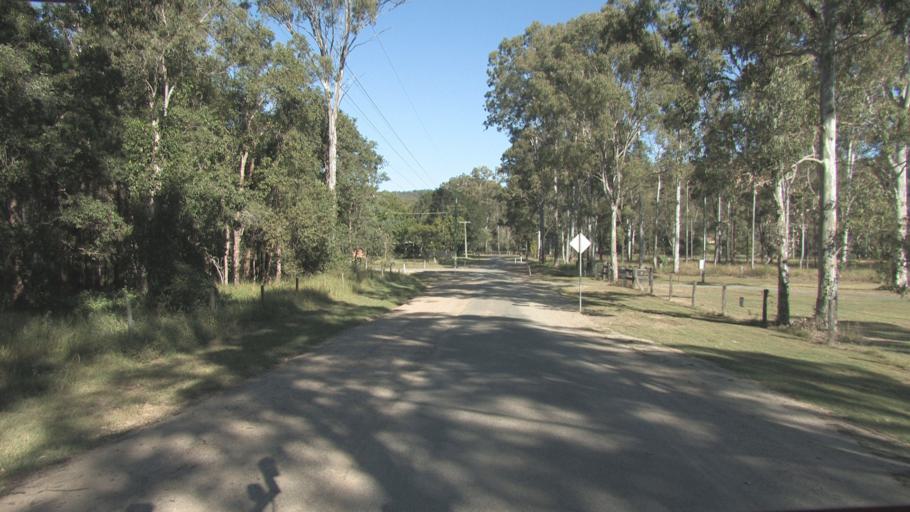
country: AU
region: Queensland
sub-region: Logan
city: Windaroo
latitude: -27.7603
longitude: 153.1510
